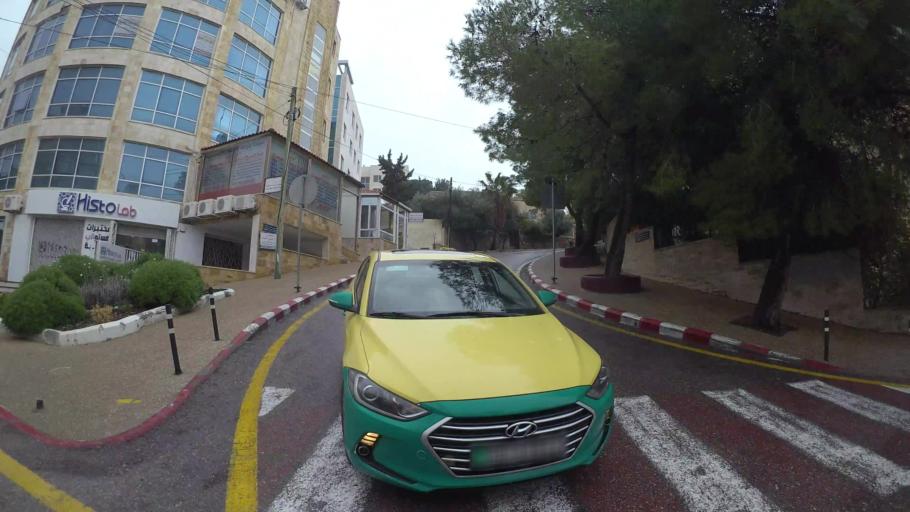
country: JO
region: Amman
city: Amman
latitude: 31.9525
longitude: 35.9007
